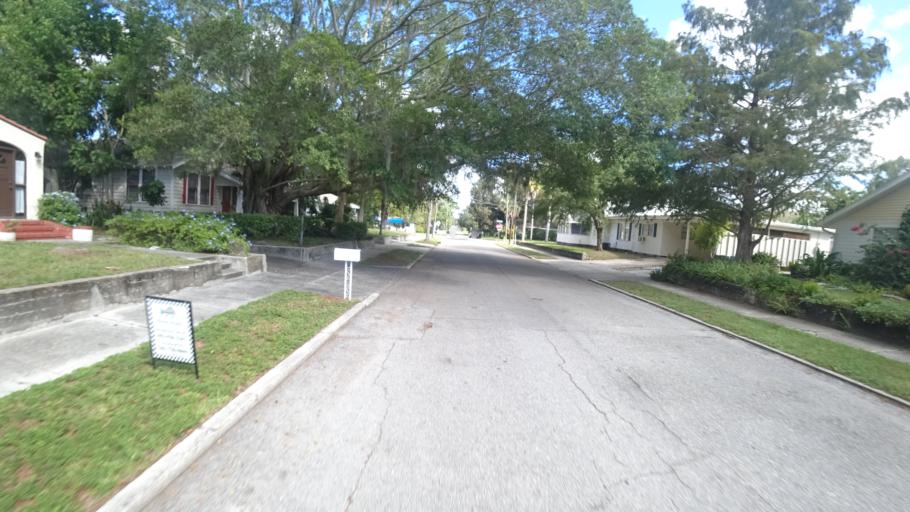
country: US
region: Florida
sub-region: Manatee County
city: Bradenton
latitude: 27.4873
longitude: -82.5840
